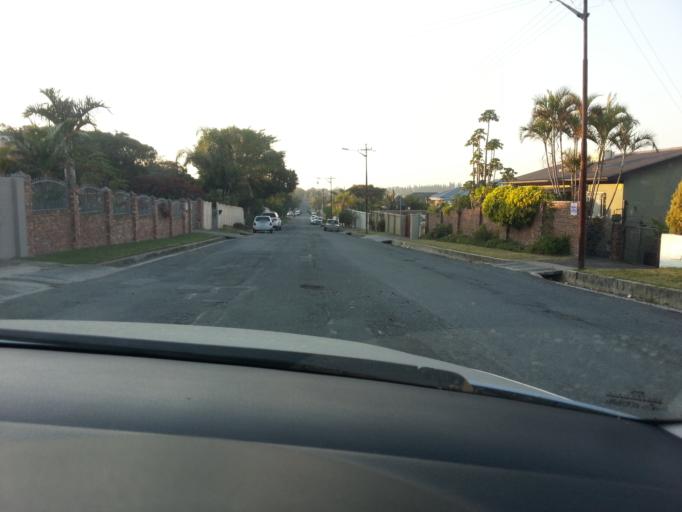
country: ZA
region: Eastern Cape
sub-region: Buffalo City Metropolitan Municipality
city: East London
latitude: -32.9870
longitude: 27.9253
